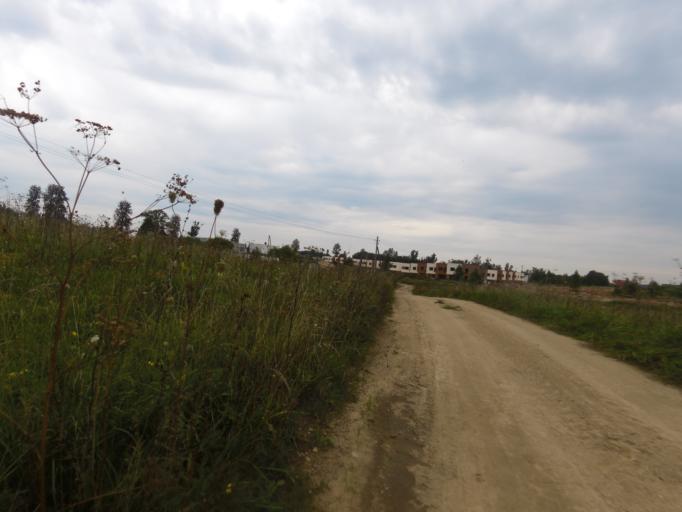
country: LT
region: Vilnius County
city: Pilaite
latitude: 54.7114
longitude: 25.1649
